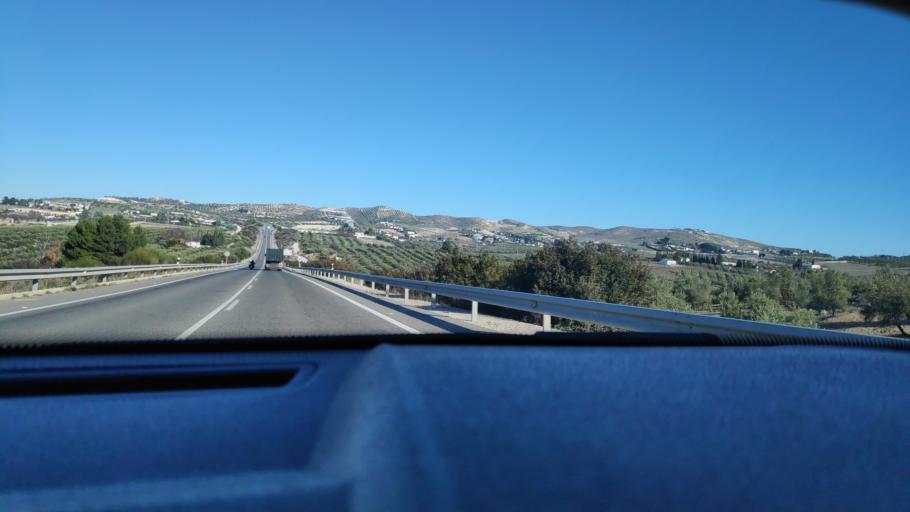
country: ES
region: Andalusia
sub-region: Province of Cordoba
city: Baena
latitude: 37.6123
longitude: -4.3008
